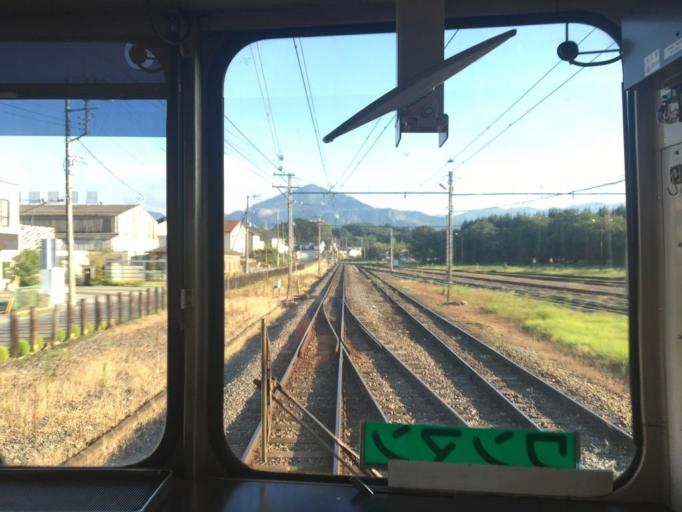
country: JP
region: Saitama
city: Chichibu
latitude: 36.0260
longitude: 139.0969
